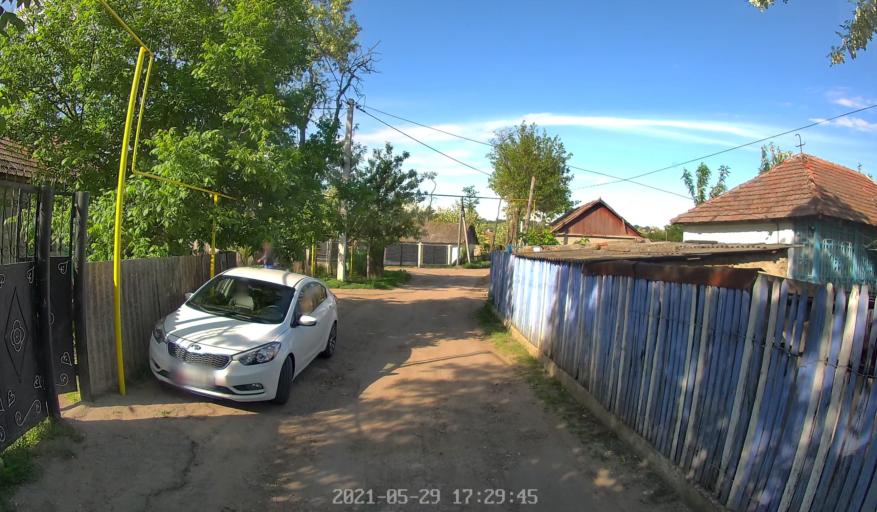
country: MD
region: Laloveni
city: Ialoveni
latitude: 46.8352
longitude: 28.8437
